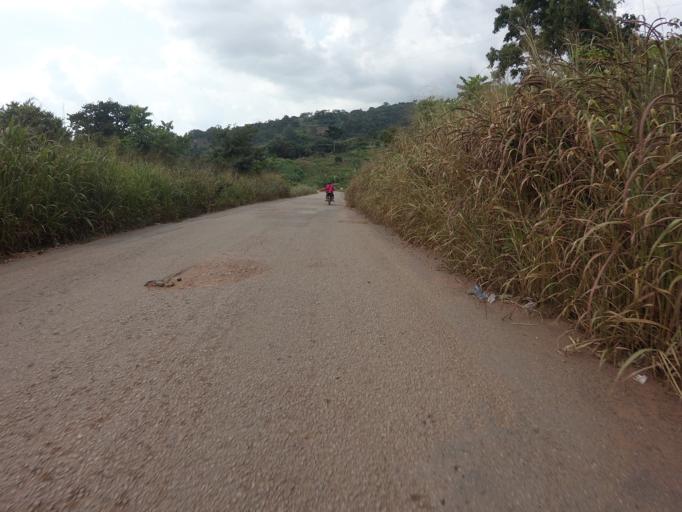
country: GH
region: Volta
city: Ho
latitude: 6.6848
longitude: 0.3481
